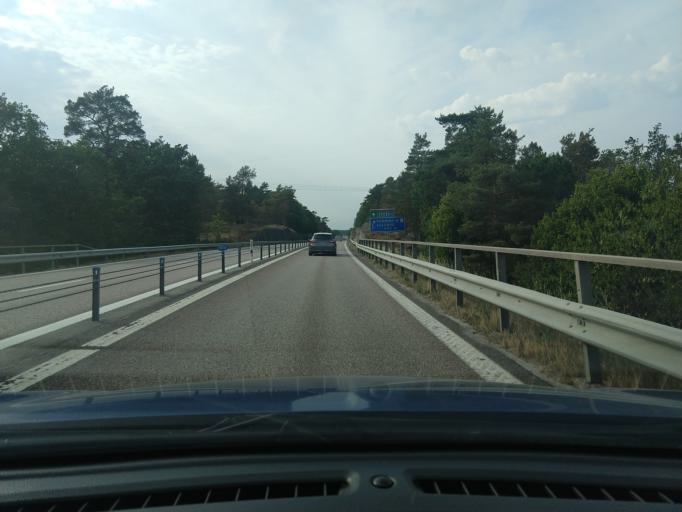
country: SE
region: Blekinge
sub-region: Ronneby Kommun
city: Ronneby
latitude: 56.2173
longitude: 15.2901
